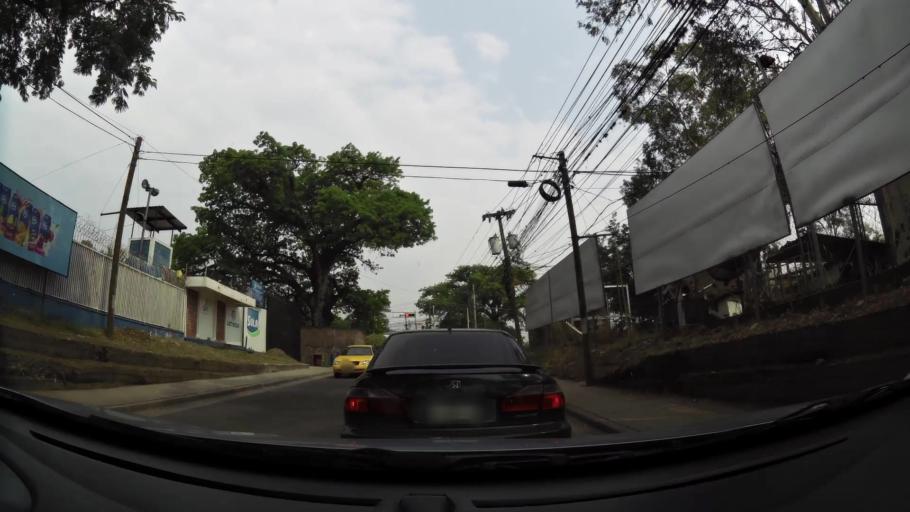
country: HN
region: Francisco Morazan
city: El Tablon
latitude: 14.0542
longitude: -87.1806
